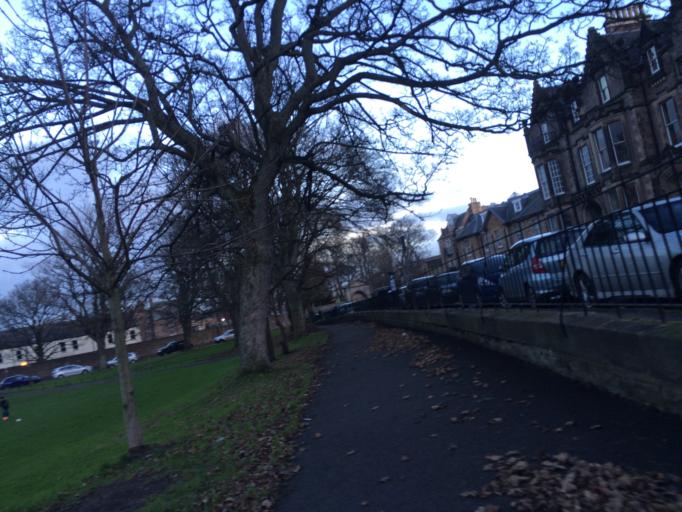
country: GB
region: Scotland
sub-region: Edinburgh
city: Edinburgh
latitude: 55.9364
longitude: -3.2038
